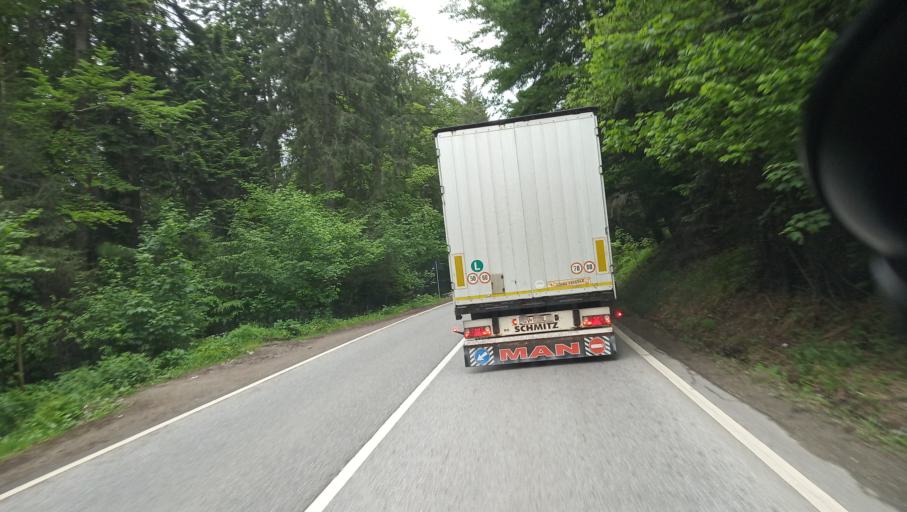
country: RO
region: Neamt
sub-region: Comuna Pipirig
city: Dolhesti
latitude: 47.1663
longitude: 26.0101
